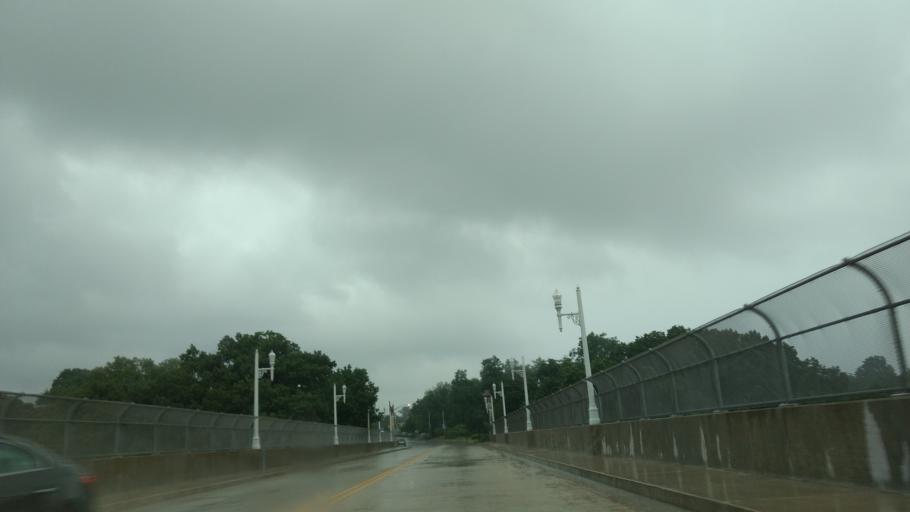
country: US
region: Pennsylvania
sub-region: Allegheny County
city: Bellevue
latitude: 40.4885
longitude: -80.0462
